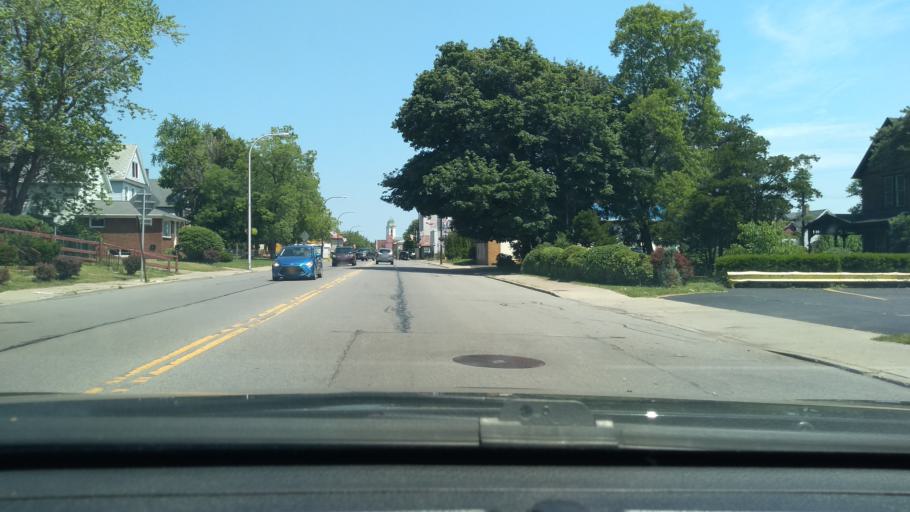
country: US
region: New York
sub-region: Erie County
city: Lackawanna
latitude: 42.8258
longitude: -78.8309
